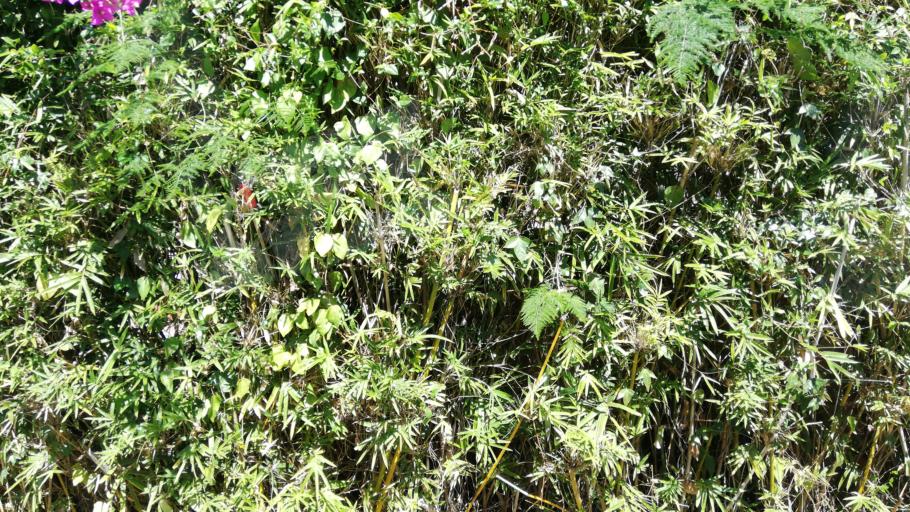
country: MU
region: Plaines Wilhems
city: Ebene
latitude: -20.2296
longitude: 57.4745
